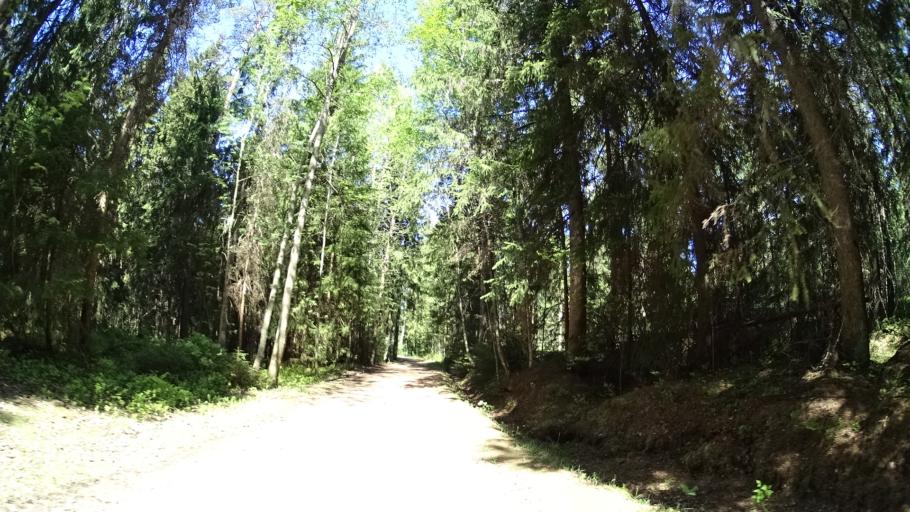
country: FI
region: Uusimaa
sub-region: Helsinki
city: Espoo
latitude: 60.1730
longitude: 24.6257
